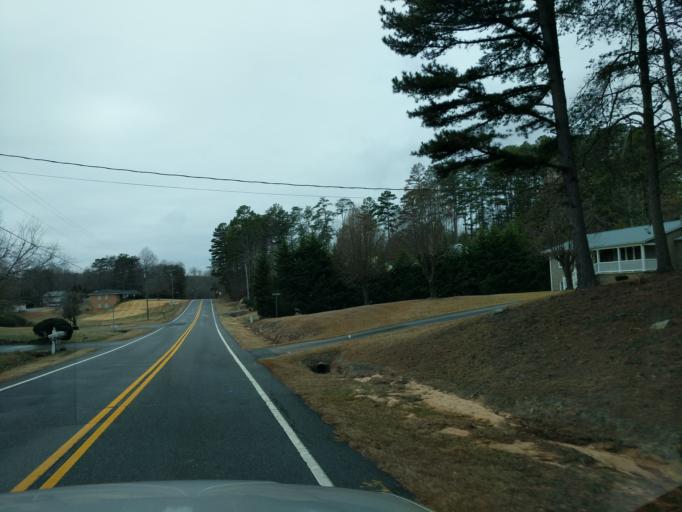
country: US
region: South Carolina
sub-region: Oconee County
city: Walhalla
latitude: 34.8099
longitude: -83.0528
